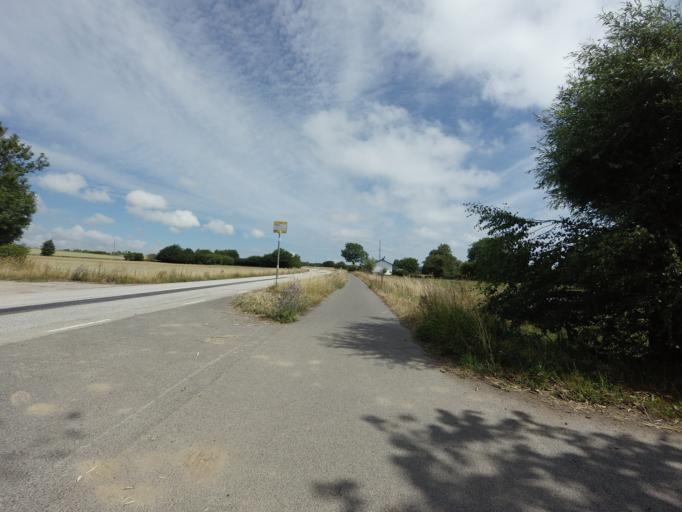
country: SE
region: Skane
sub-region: Simrishamns Kommun
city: Simrishamn
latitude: 55.5084
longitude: 14.3348
